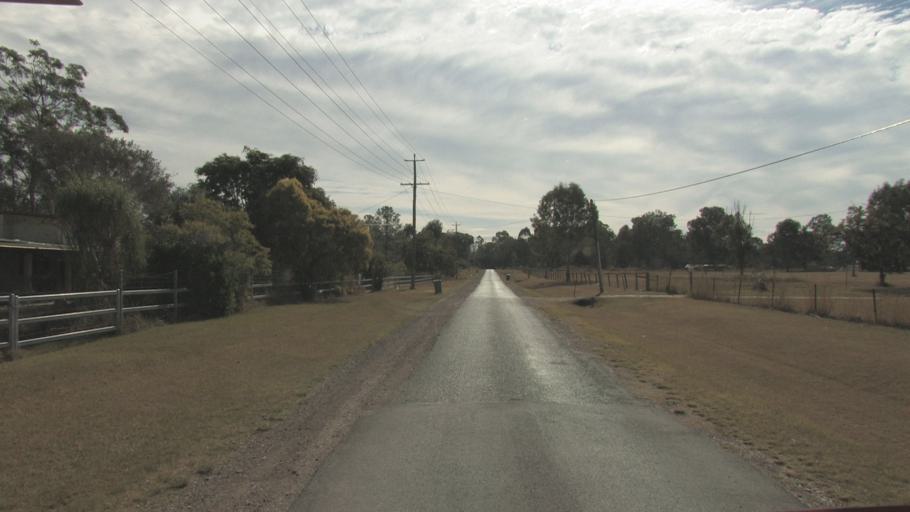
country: AU
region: Queensland
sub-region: Logan
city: North Maclean
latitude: -27.7785
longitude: 153.0080
